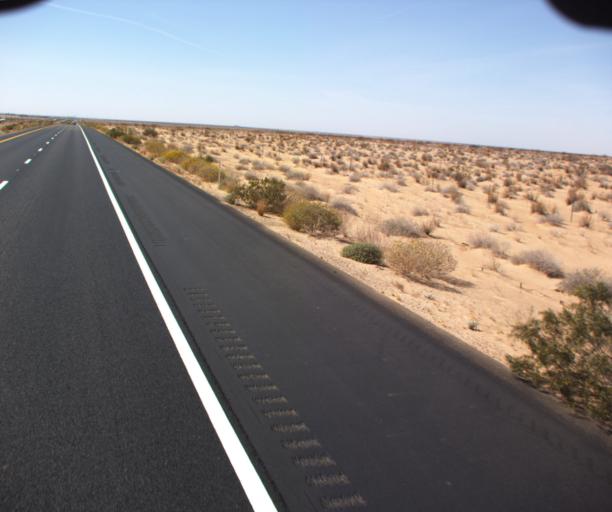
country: US
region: Arizona
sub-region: Yuma County
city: Somerton
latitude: 32.4954
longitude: -114.6076
